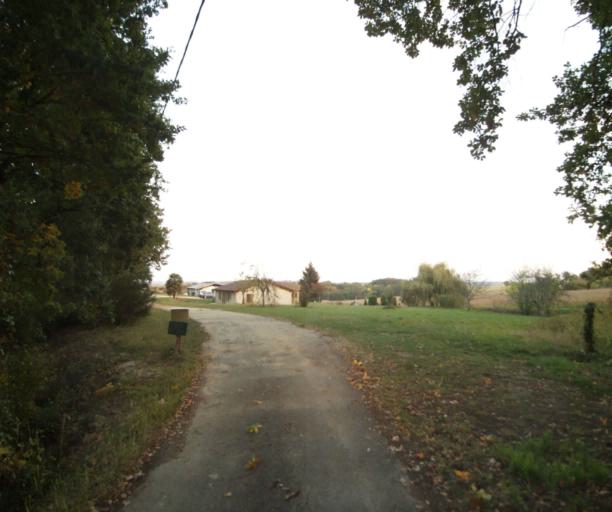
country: FR
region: Midi-Pyrenees
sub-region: Departement du Gers
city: Vic-Fezensac
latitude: 43.8012
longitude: 0.2426
